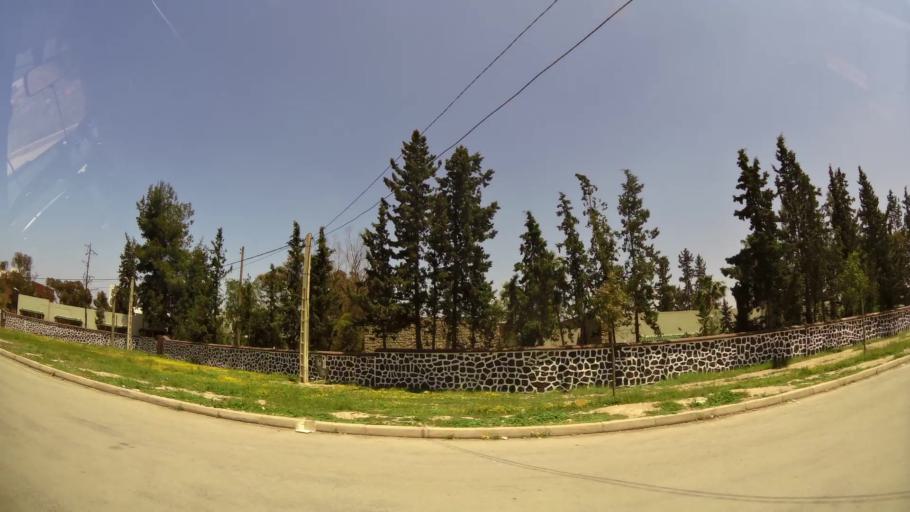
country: MA
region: Oriental
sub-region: Oujda-Angad
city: Oujda
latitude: 34.6912
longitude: -1.8991
